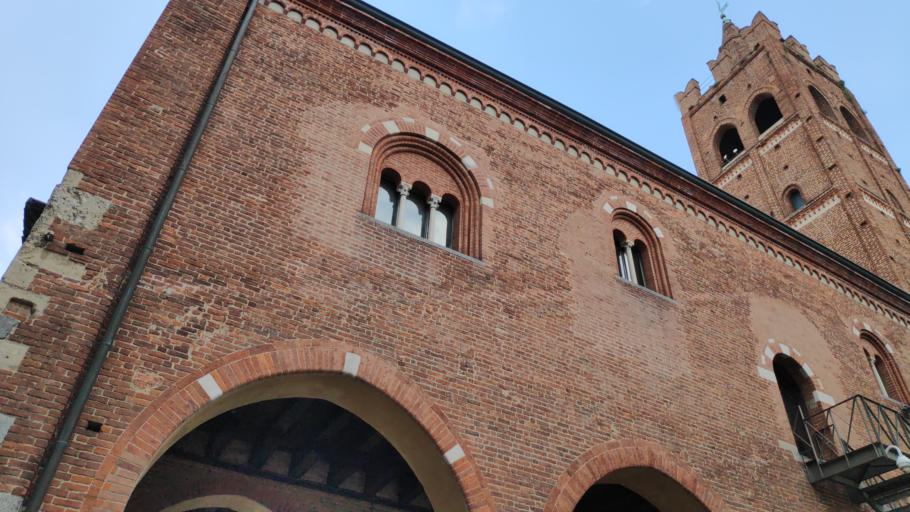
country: IT
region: Lombardy
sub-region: Provincia di Monza e Brianza
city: Monza
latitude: 45.5843
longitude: 9.2752
